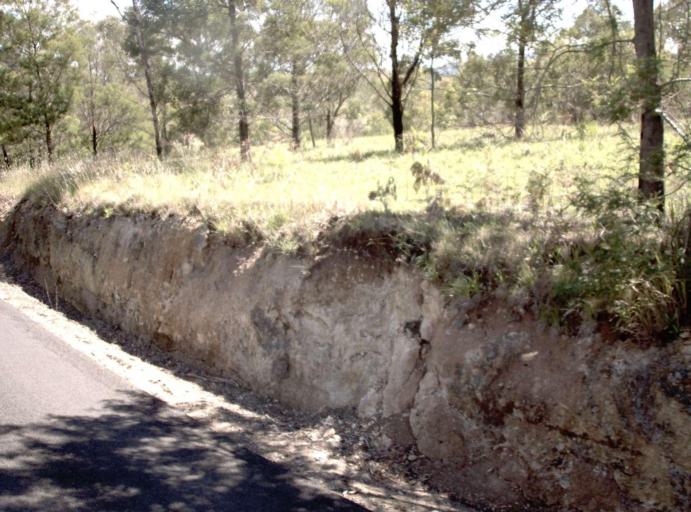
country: AU
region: Victoria
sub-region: East Gippsland
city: Lakes Entrance
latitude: -37.4451
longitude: 148.1908
